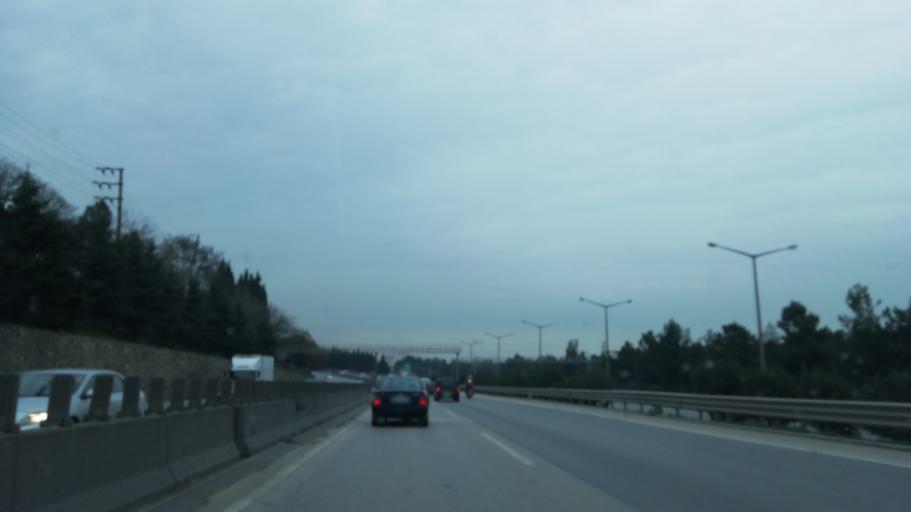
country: TR
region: Kocaeli
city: Izmit
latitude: 40.7616
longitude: 29.8696
